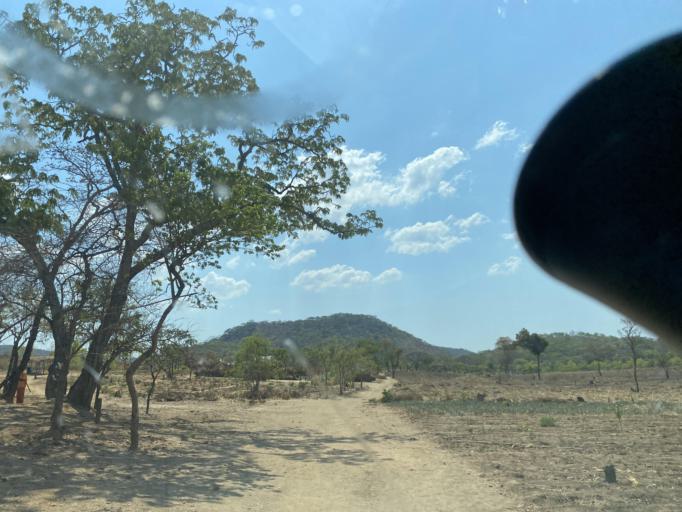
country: ZM
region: Lusaka
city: Chongwe
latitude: -15.0836
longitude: 29.4739
